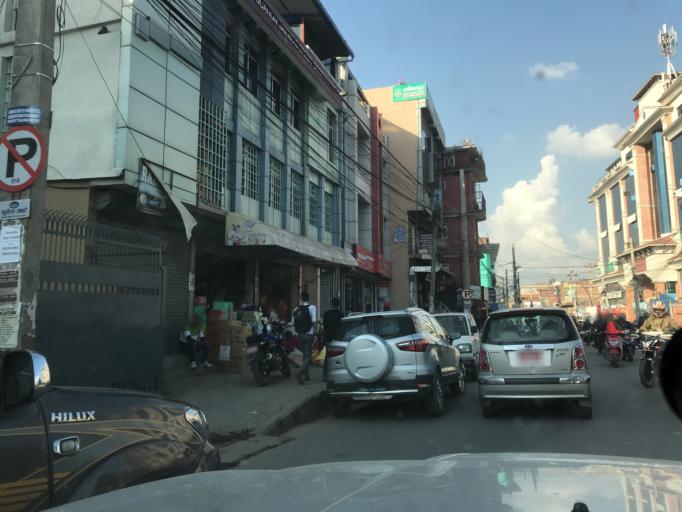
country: NP
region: Central Region
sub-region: Bagmati Zone
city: Patan
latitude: 27.6669
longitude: 85.3211
